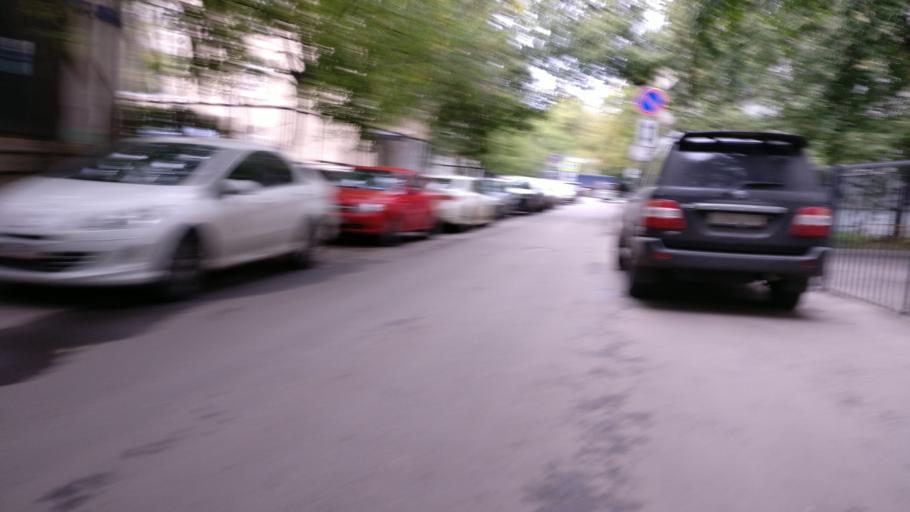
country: RU
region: Moscow
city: Sokol'niki
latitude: 55.7755
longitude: 37.6455
